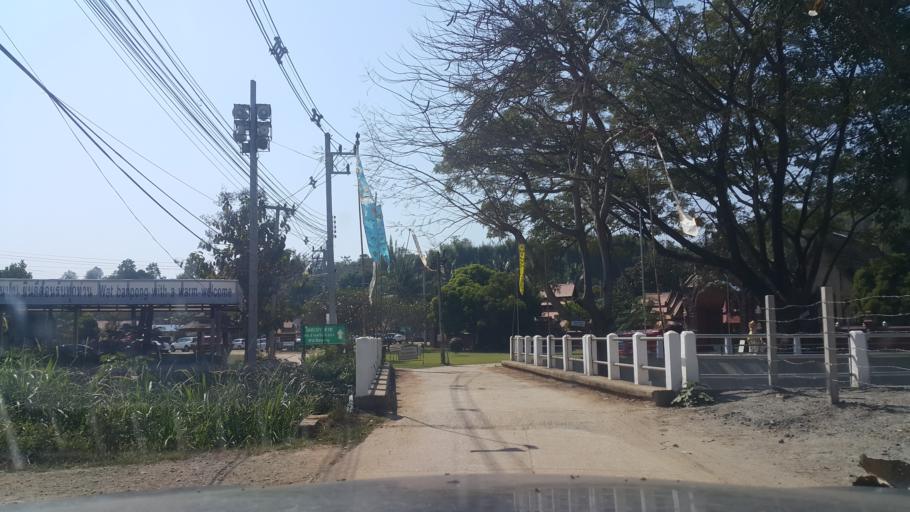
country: TH
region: Chiang Mai
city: Hang Dong
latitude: 18.7499
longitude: 98.8811
